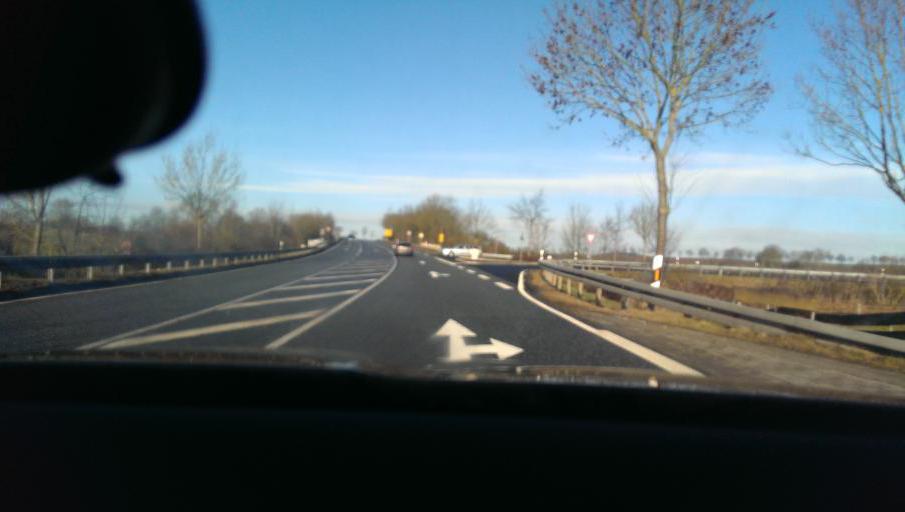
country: DE
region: Hesse
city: Hain-Grundau
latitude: 50.2364
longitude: 9.1287
